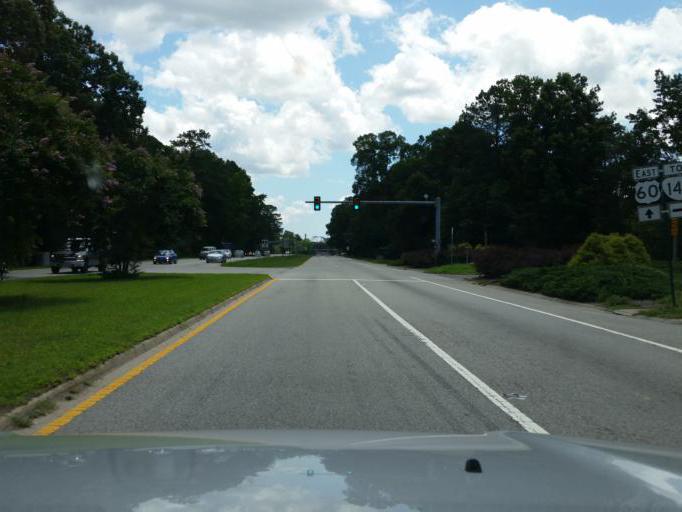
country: US
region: Virginia
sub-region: City of Williamsburg
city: Williamsburg
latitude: 37.2509
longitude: -76.6620
